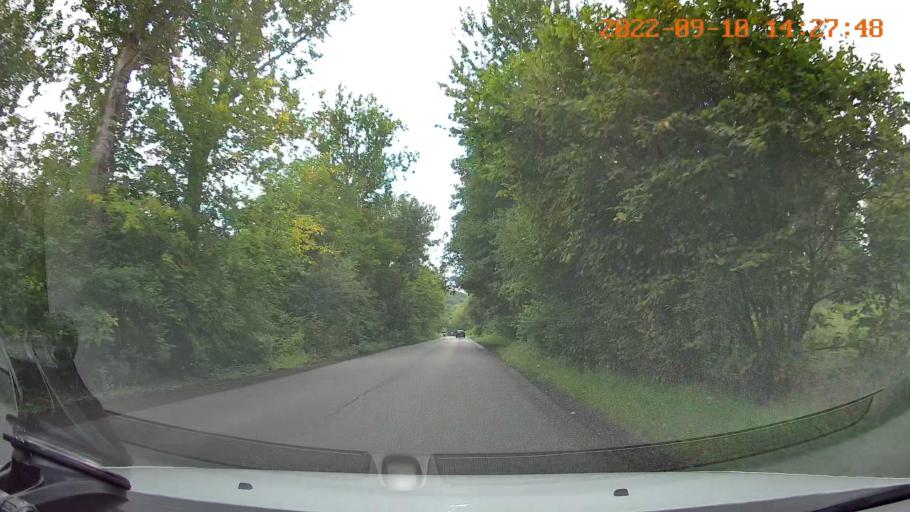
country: PL
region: Lesser Poland Voivodeship
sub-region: Powiat krakowski
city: Rzaska
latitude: 50.0708
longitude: 19.8473
